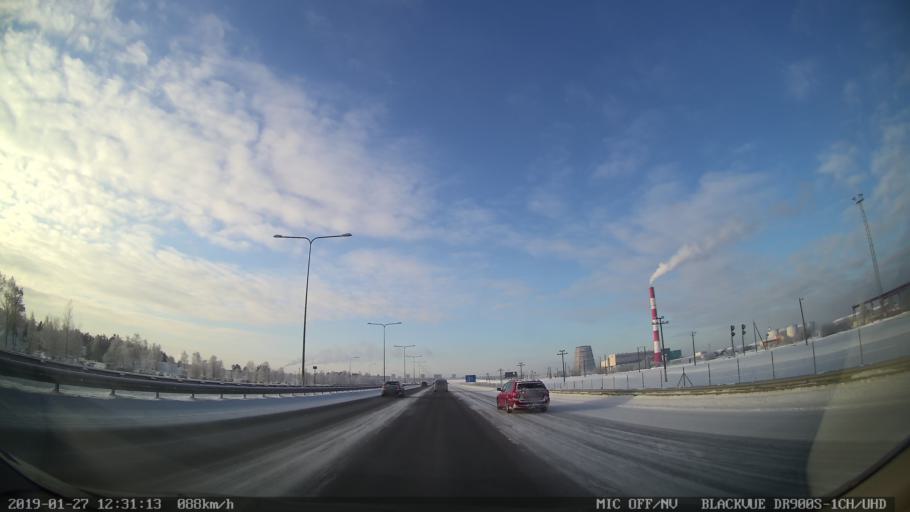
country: EE
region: Harju
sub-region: Joelaehtme vald
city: Loo
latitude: 59.4486
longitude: 24.9436
